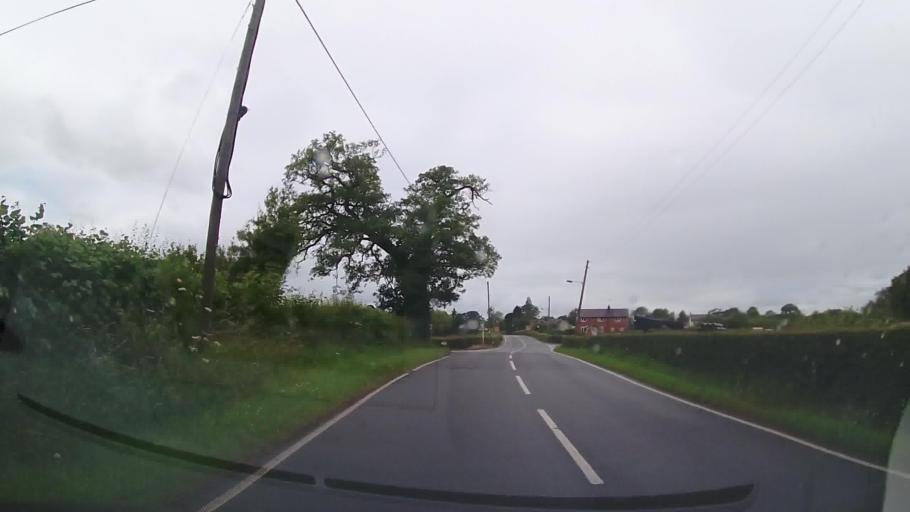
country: GB
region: Wales
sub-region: Wrexham
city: Overton
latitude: 52.9227
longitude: -2.9330
